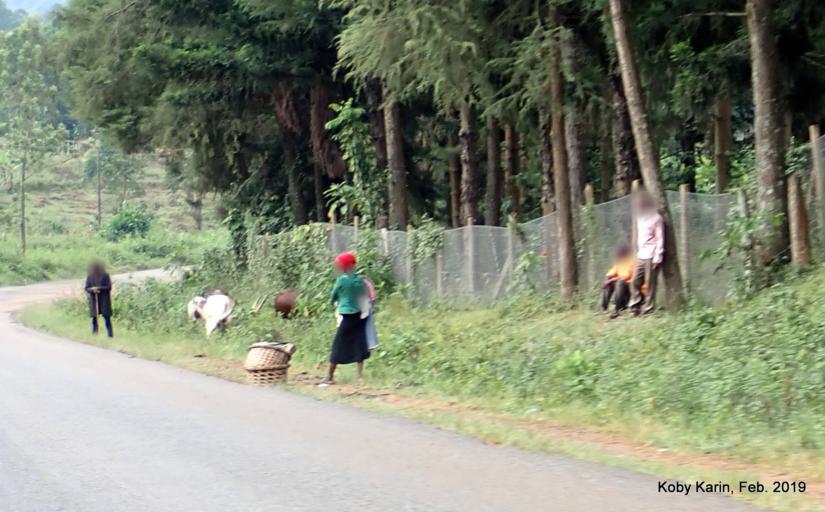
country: UG
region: Western Region
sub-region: Rubirizi District
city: Rubirizi
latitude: -0.3286
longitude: 30.1054
